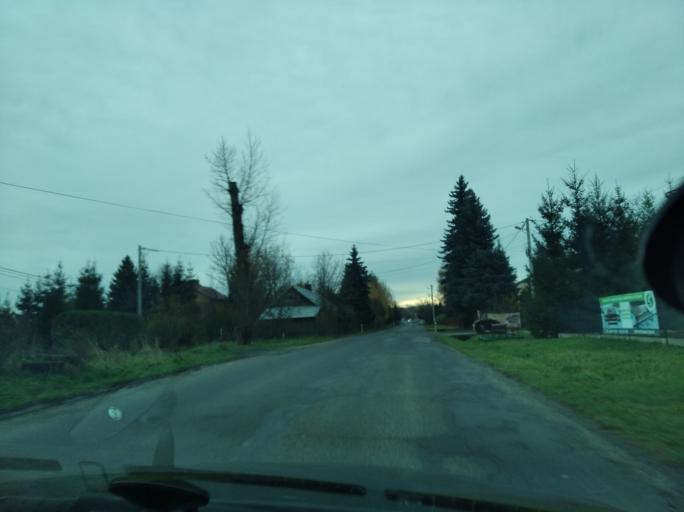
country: PL
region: Subcarpathian Voivodeship
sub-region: Powiat lancucki
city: Krzemienica
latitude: 50.0854
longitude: 22.1875
